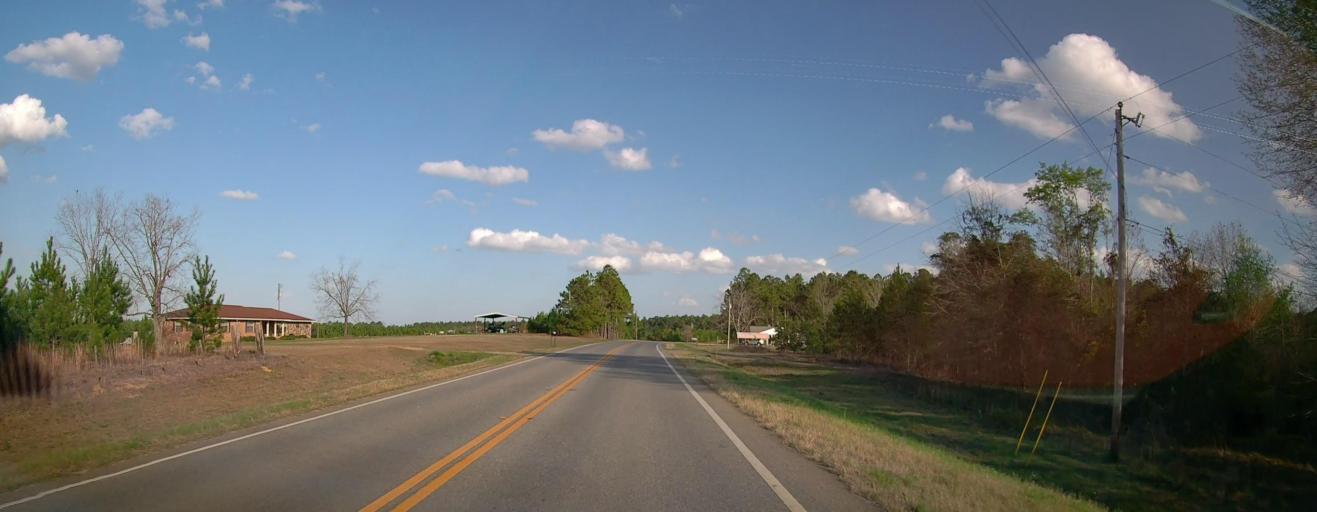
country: US
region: Georgia
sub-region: Toombs County
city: Lyons
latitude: 32.1747
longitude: -82.2809
